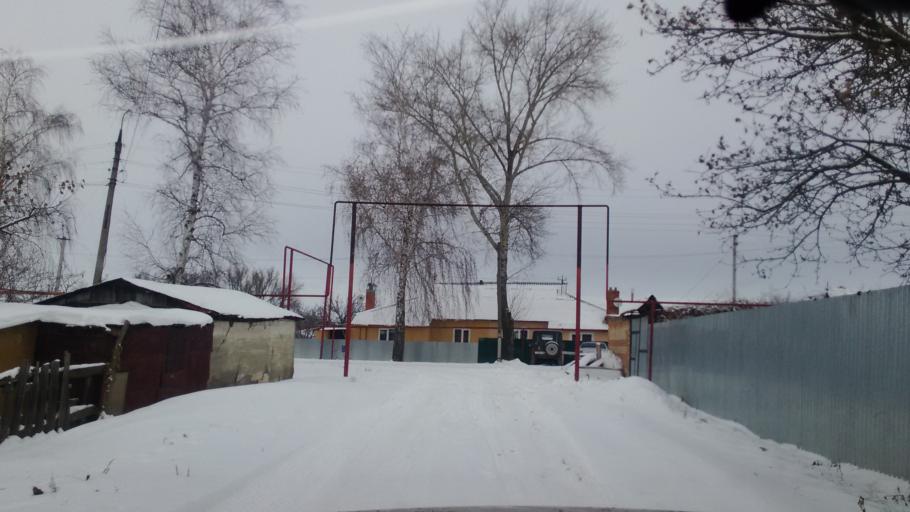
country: RU
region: Tula
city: Bogoroditsk
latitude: 53.7579
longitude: 38.1127
